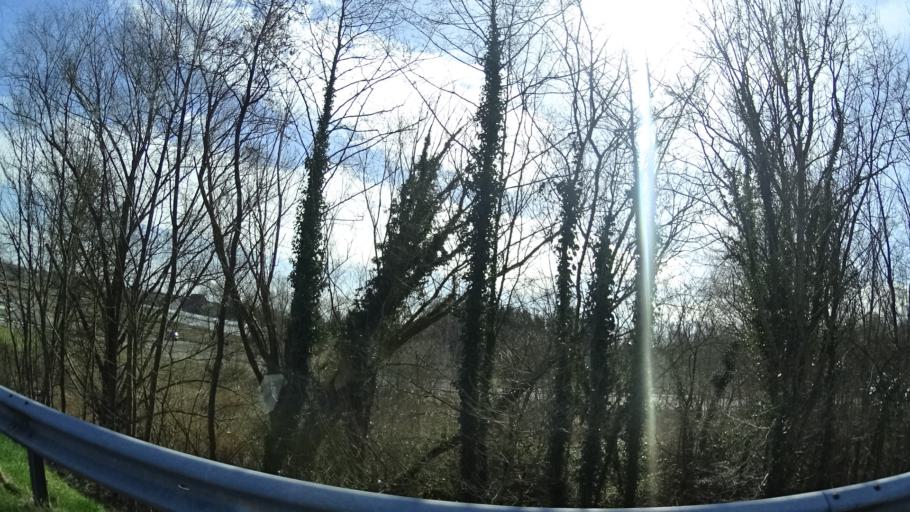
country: DE
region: Rheinland-Pfalz
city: Hanhofen
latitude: 49.3172
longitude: 8.3355
